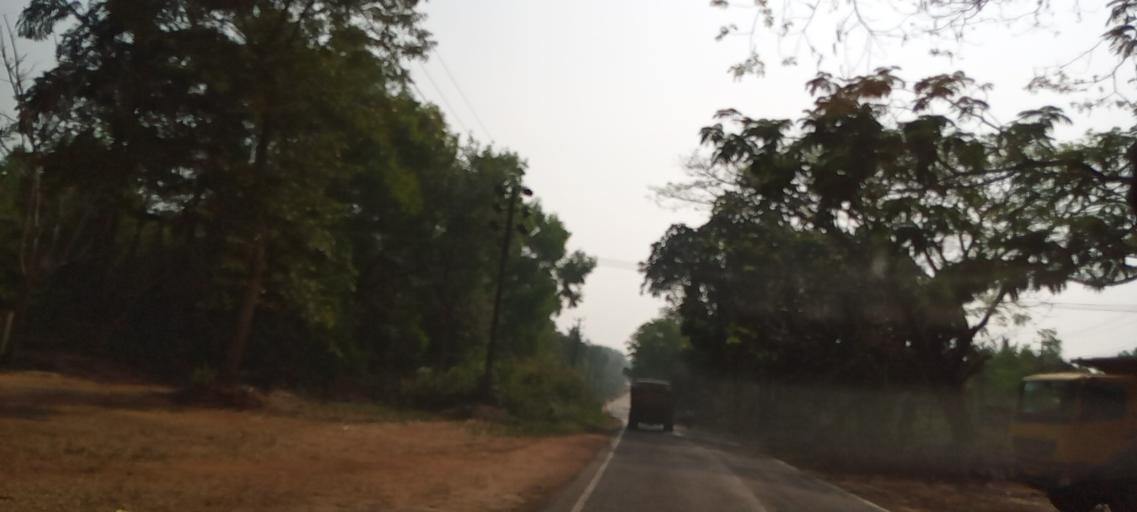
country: IN
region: Karnataka
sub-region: Udupi
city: Coondapoor
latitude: 13.5159
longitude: 74.7482
